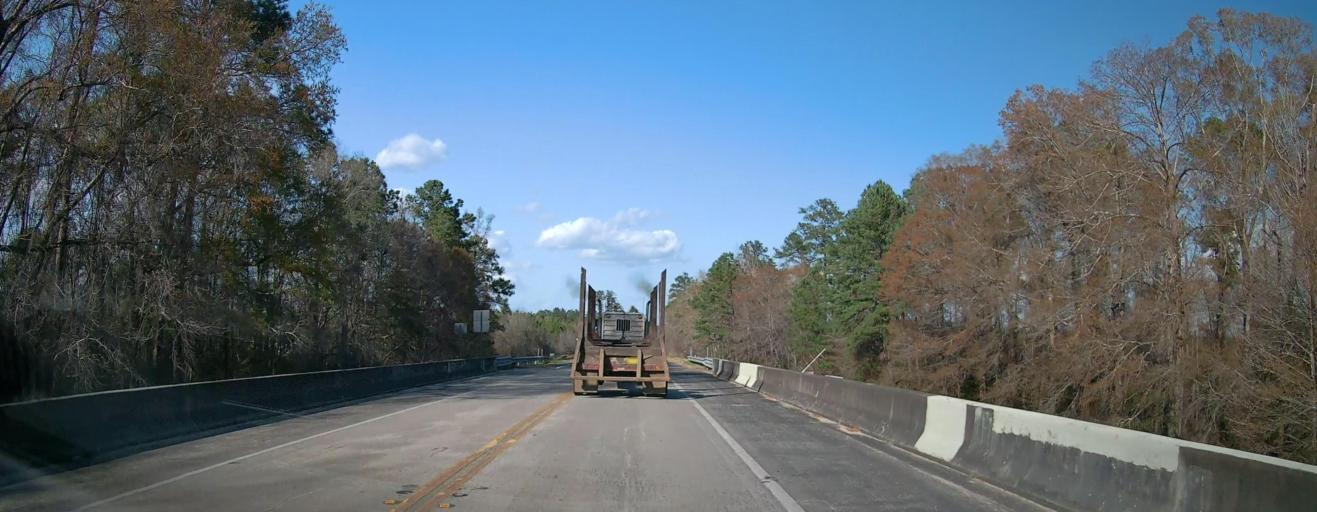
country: US
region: Georgia
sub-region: Telfair County
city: McRae
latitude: 32.0524
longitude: -82.8156
